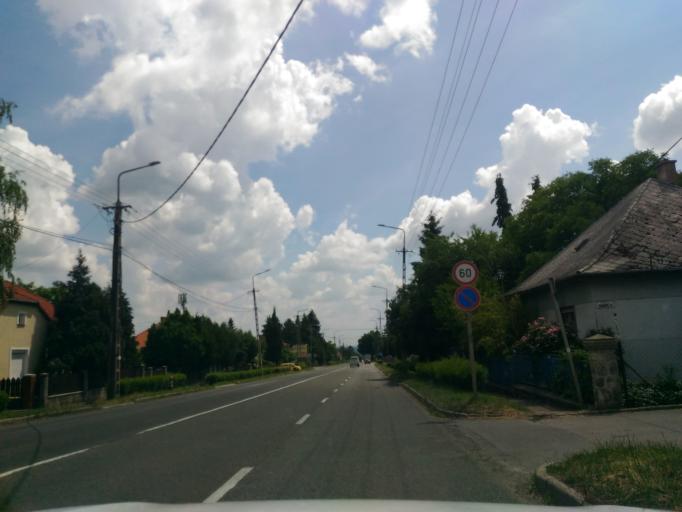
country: HU
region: Baranya
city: Pecs
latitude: 46.1089
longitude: 18.2629
